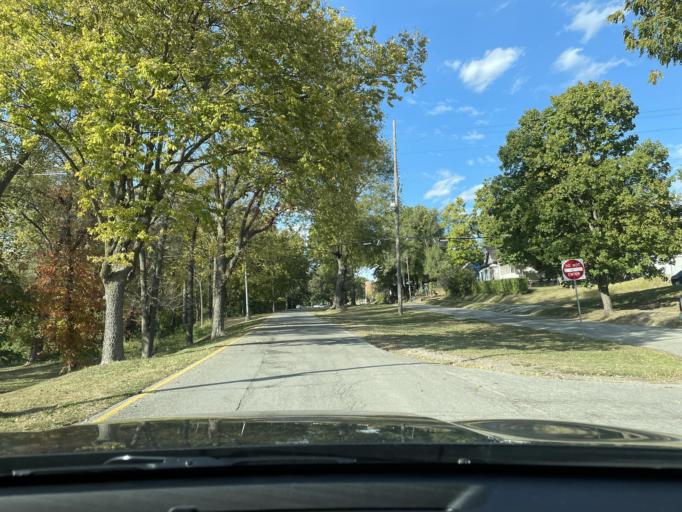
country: US
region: Kansas
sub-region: Doniphan County
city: Elwood
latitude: 39.7121
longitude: -94.8554
